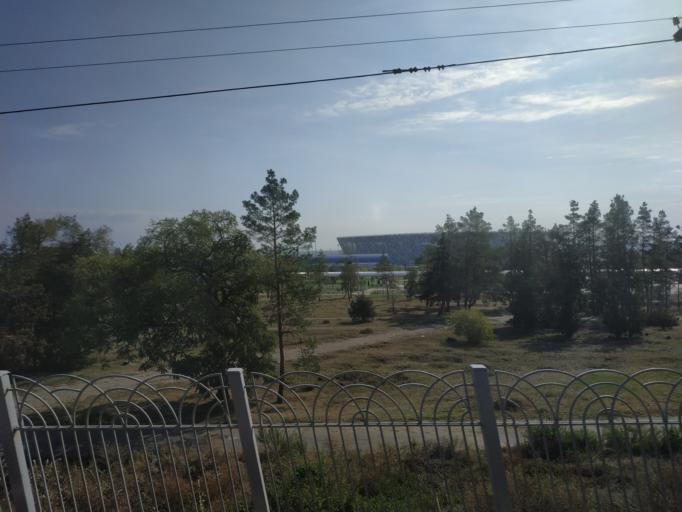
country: RU
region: Volgograd
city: Volgograd
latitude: 48.7379
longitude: 44.5409
